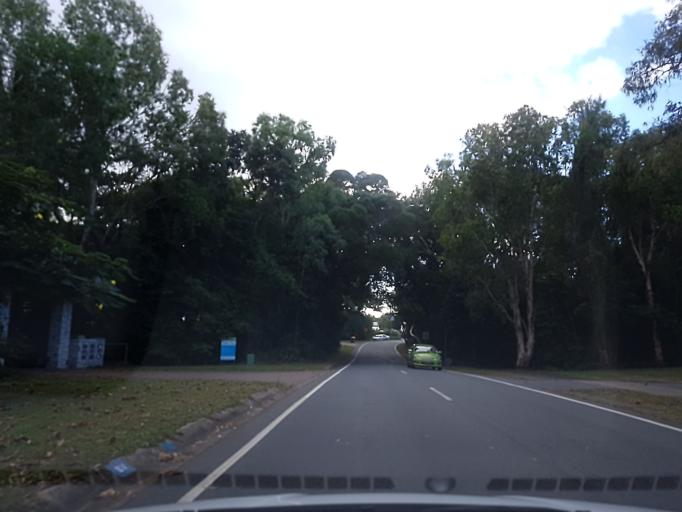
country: AU
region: Queensland
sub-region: Cairns
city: Palm Cove
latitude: -16.7630
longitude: 145.6736
